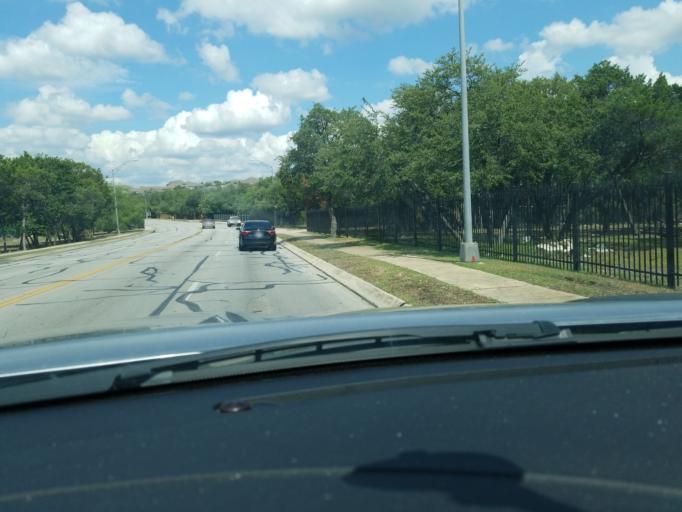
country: US
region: Texas
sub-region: Bexar County
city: Timberwood Park
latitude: 29.6861
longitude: -98.4622
